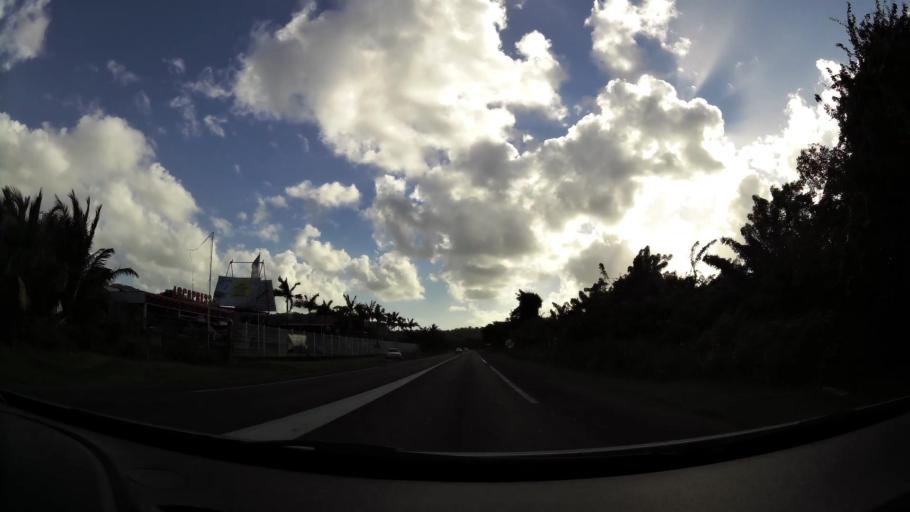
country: MQ
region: Martinique
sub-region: Martinique
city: Ducos
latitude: 14.5998
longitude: -60.9712
